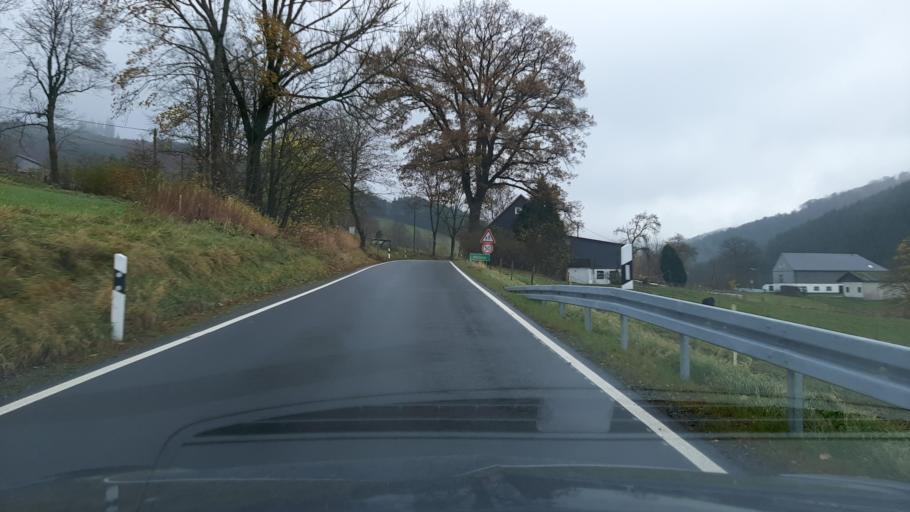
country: DE
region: North Rhine-Westphalia
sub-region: Regierungsbezirk Arnsberg
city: Bad Fredeburg
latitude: 51.1925
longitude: 8.3771
